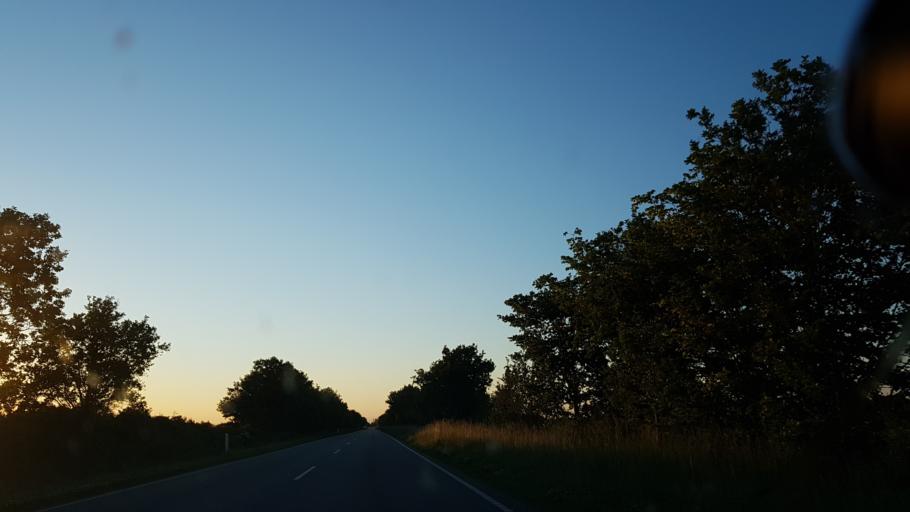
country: DK
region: South Denmark
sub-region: Aabenraa Kommune
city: Krusa
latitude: 54.9277
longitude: 9.3703
